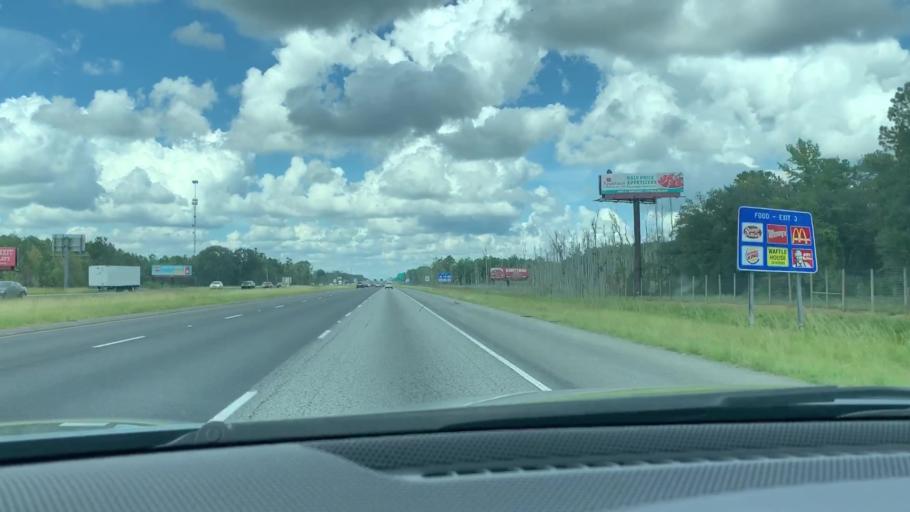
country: US
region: Georgia
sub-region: Camden County
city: Kingsland
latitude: 30.7695
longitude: -81.6543
